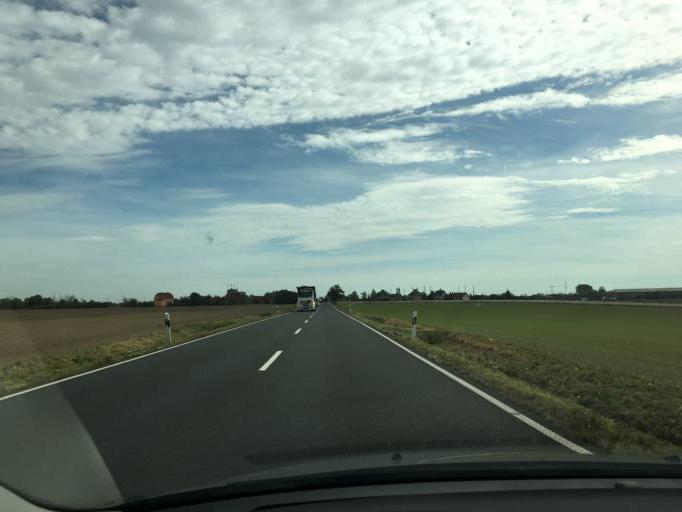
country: DE
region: Saxony
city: Lommatzsch
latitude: 51.2488
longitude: 13.2943
